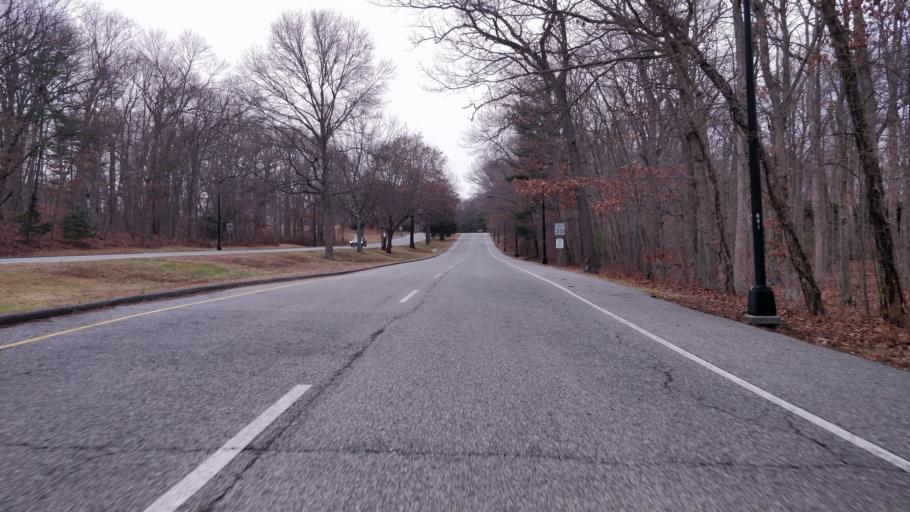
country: US
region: New York
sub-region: Nassau County
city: Brookville
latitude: 40.7973
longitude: -73.5661
